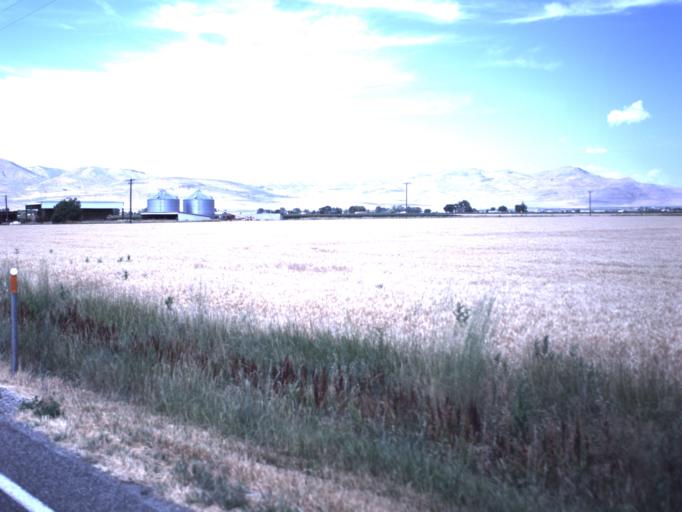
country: US
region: Utah
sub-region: Box Elder County
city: Tremonton
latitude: 41.7101
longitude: -112.2370
